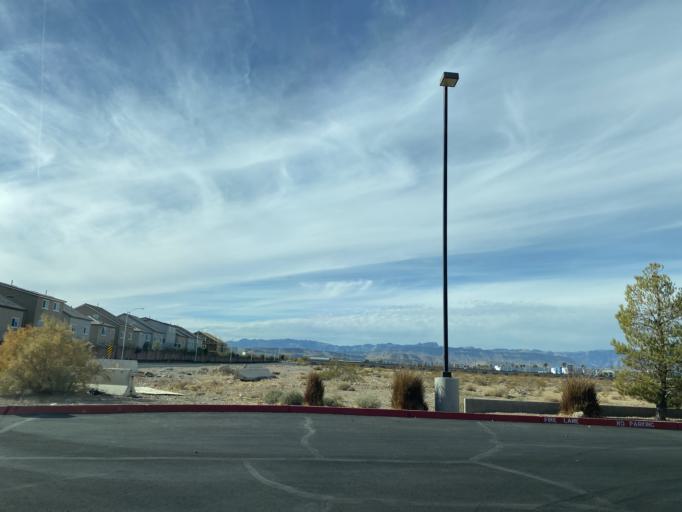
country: US
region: Nevada
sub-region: Clark County
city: Enterprise
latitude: 36.0620
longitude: -115.2290
